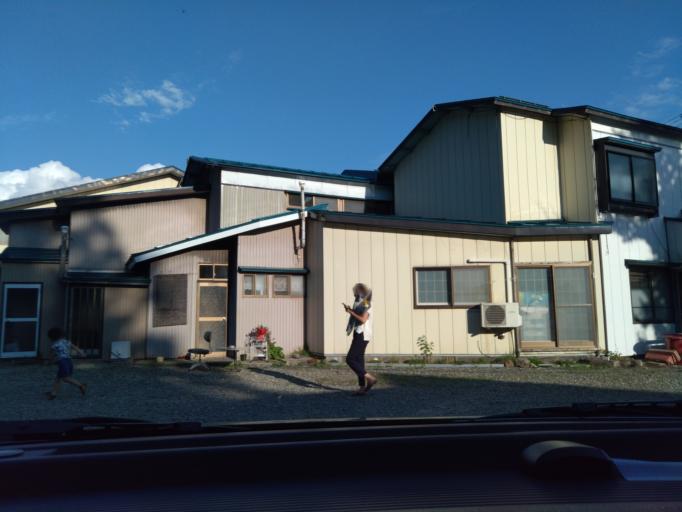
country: JP
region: Akita
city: Kakunodatemachi
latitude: 39.5852
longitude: 140.5685
